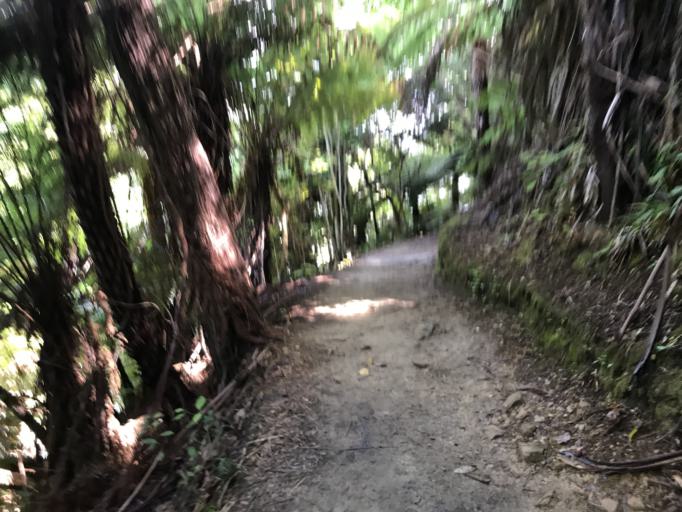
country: NZ
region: Marlborough
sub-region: Marlborough District
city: Picton
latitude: -41.2585
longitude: 173.9350
